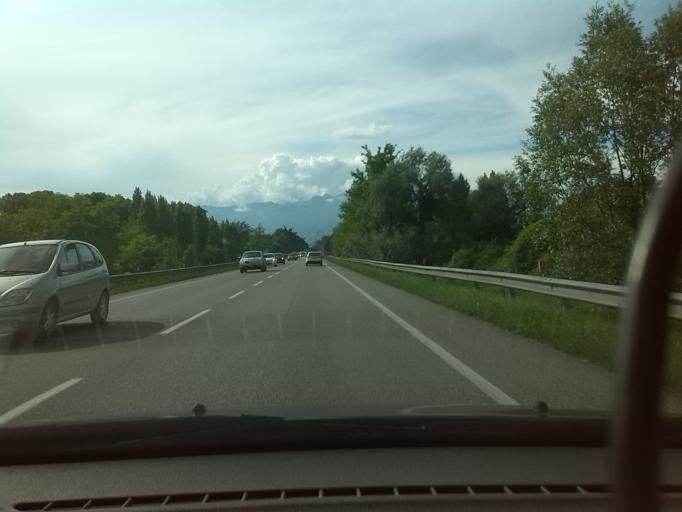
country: IT
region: Friuli Venezia Giulia
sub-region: Provincia di Pordenone
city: Pordenone
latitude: 45.9585
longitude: 12.6802
